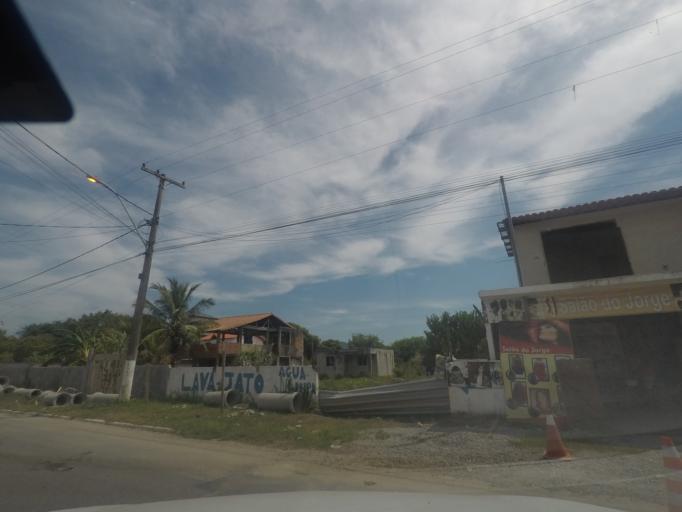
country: BR
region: Rio de Janeiro
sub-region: Marica
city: Marica
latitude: -22.9511
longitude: -42.7492
